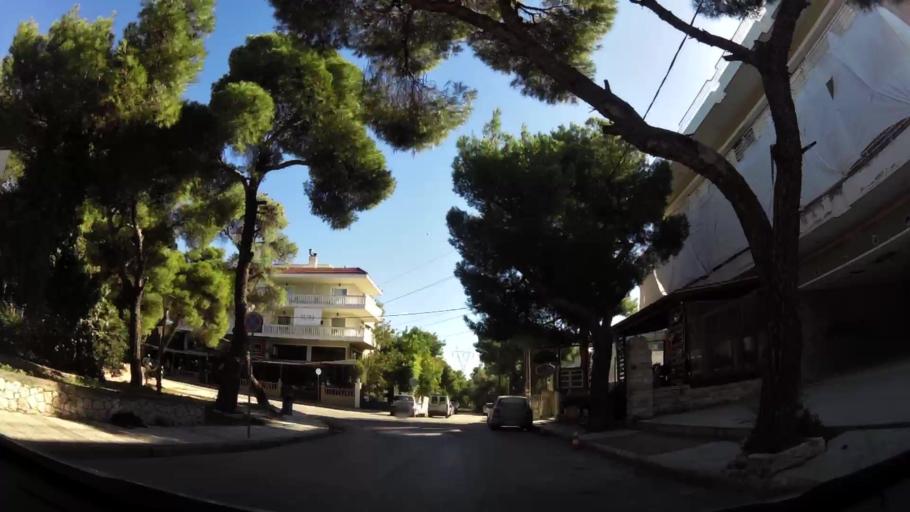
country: GR
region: Attica
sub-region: Nomarchia Anatolikis Attikis
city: Varybobi
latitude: 38.1293
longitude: 23.7894
